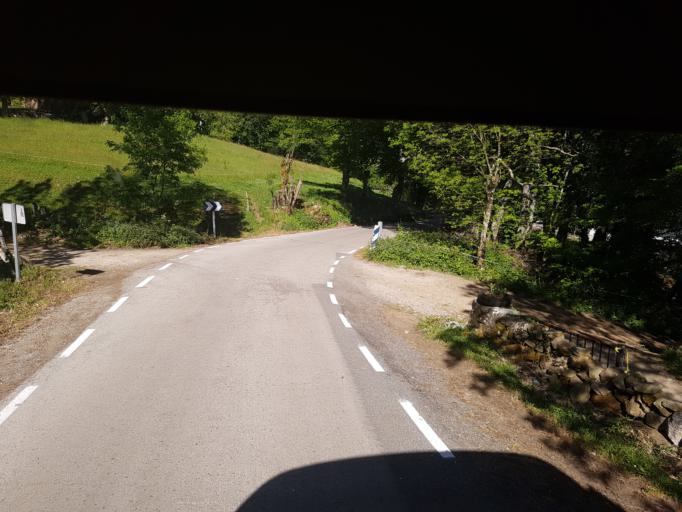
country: ES
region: Castille and Leon
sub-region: Provincia de Burgos
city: Espinosa de los Monteros
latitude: 43.1251
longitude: -3.5804
